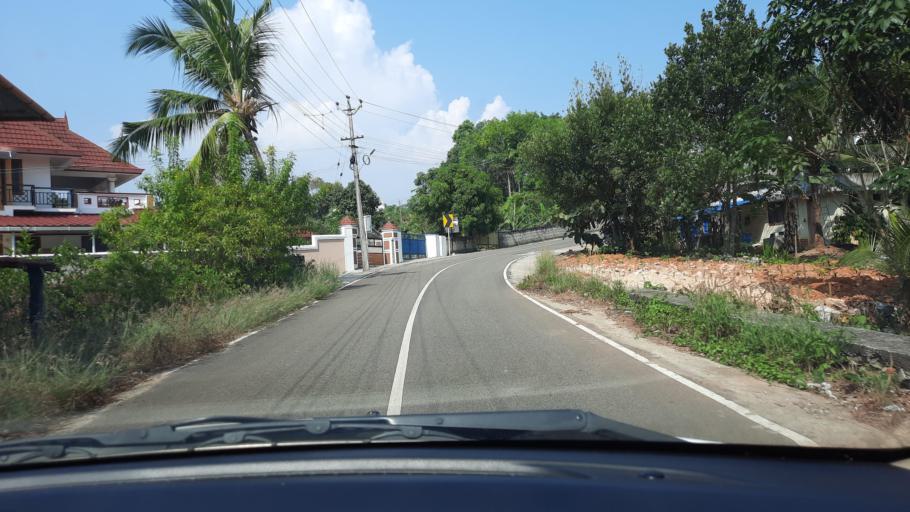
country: IN
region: Kerala
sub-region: Thiruvananthapuram
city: Nedumangad
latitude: 8.5891
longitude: 76.9283
